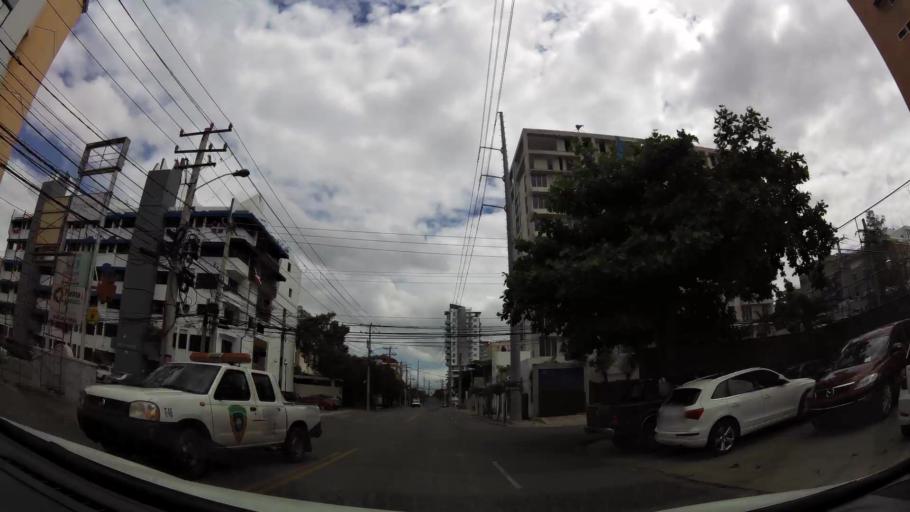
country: DO
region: Nacional
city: La Julia
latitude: 18.4802
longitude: -69.9408
